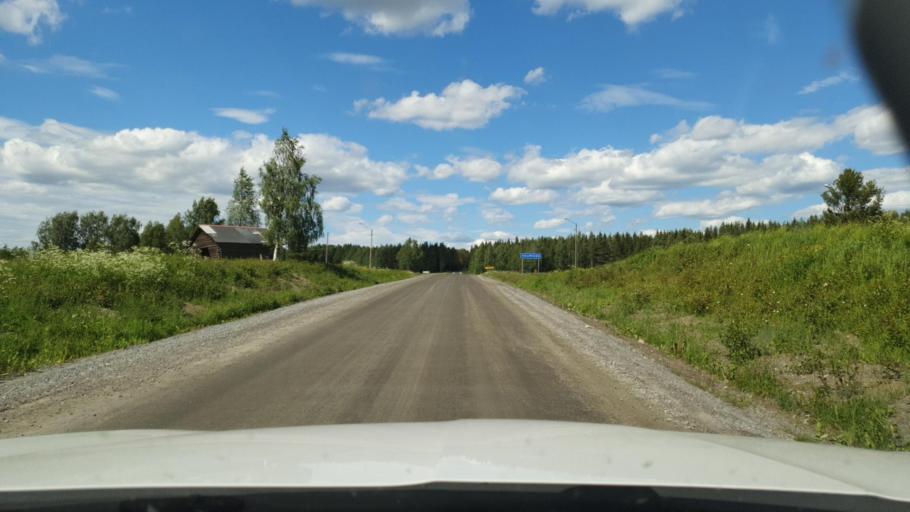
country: SE
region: Vaesterbotten
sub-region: Skelleftea Kommun
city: Forsbacka
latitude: 64.7888
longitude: 20.5105
